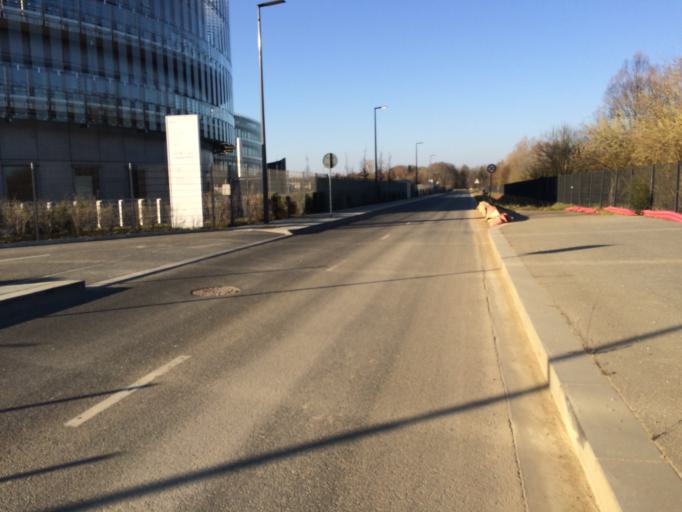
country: FR
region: Ile-de-France
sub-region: Departement de l'Essonne
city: Vauhallan
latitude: 48.7160
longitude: 2.1985
